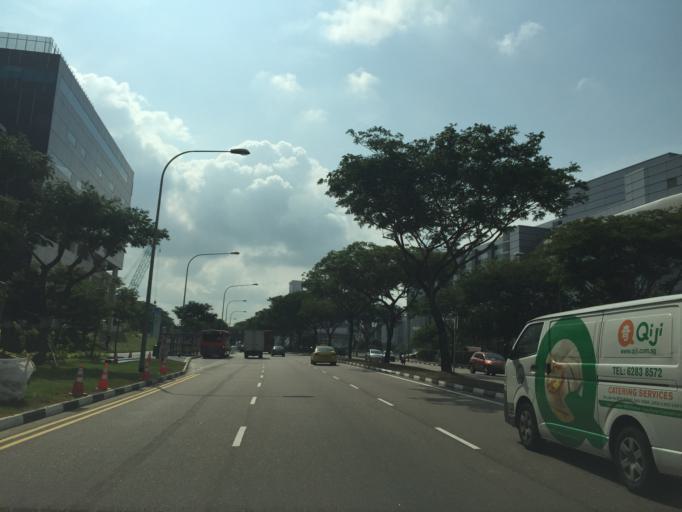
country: SG
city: Singapore
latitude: 1.3338
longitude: 103.8897
